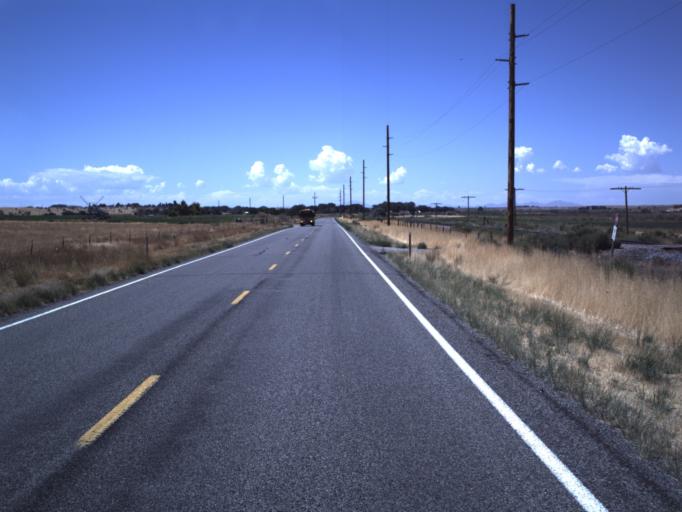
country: US
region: Utah
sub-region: Millard County
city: Delta
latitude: 39.5388
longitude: -112.2527
